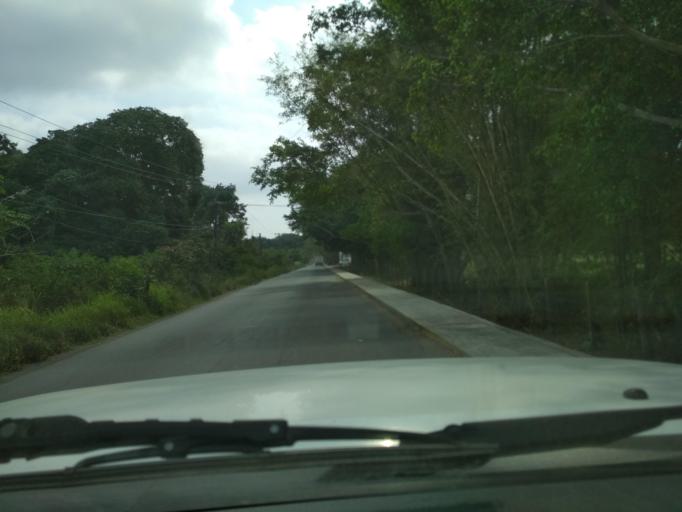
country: MX
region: Veracruz
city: El Tejar
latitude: 19.0791
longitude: -96.1755
